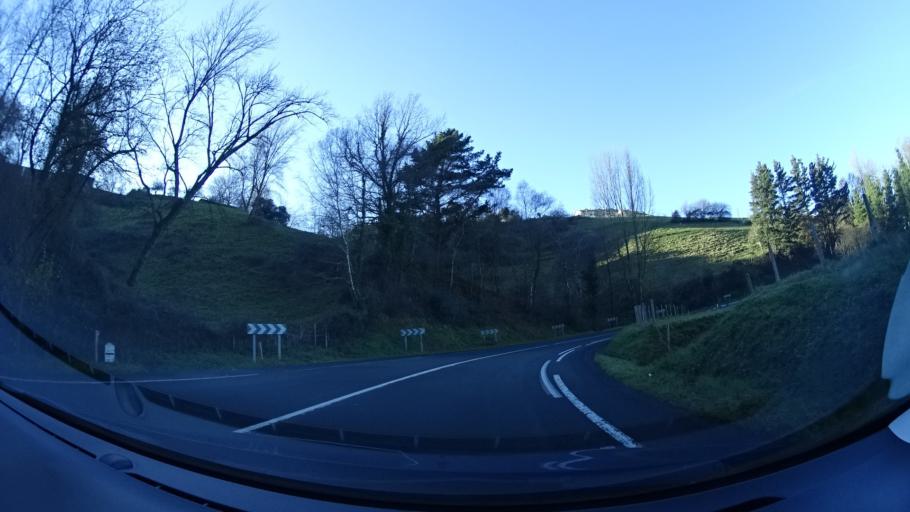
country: ES
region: Basque Country
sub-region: Provincia de Guipuzcoa
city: Deba
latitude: 43.2681
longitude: -2.3245
